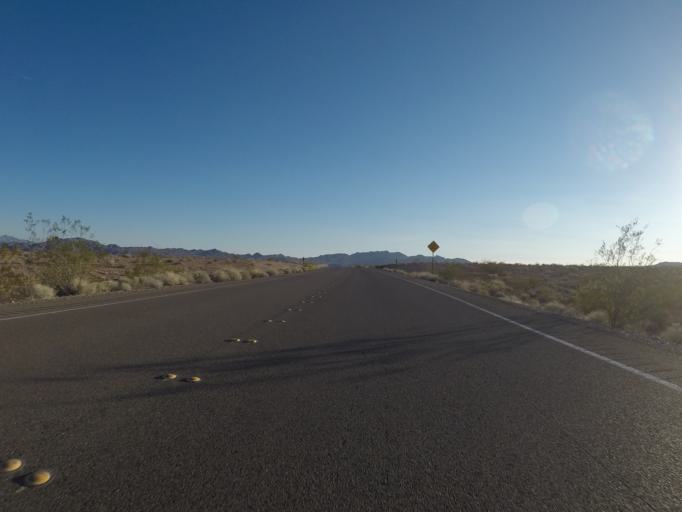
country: US
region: Nevada
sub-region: Clark County
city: Moapa Valley
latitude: 36.3311
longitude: -114.4928
